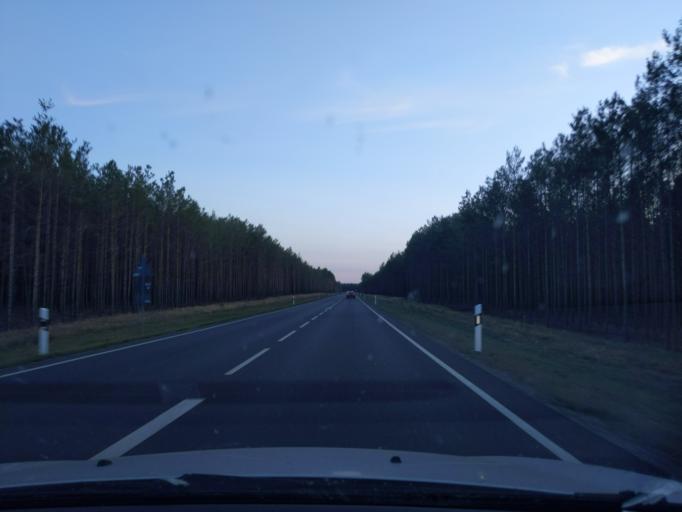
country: DE
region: Saxony
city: Wittichenau
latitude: 51.4199
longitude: 14.2946
